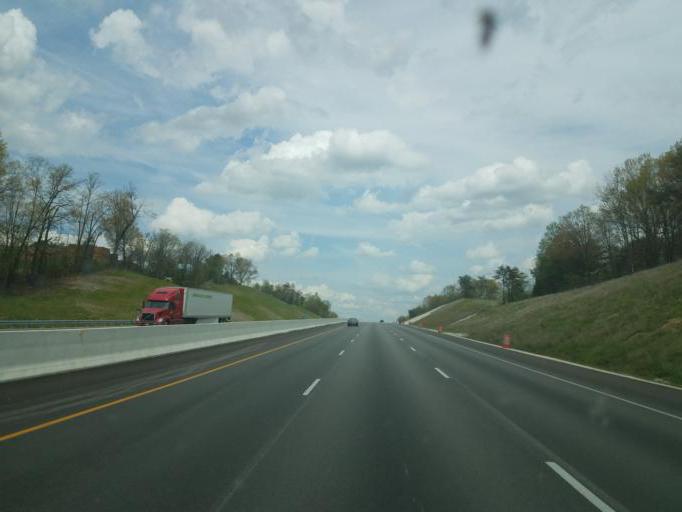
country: US
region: Kentucky
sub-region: Hart County
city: Munfordville
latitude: 37.3205
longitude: -85.9057
